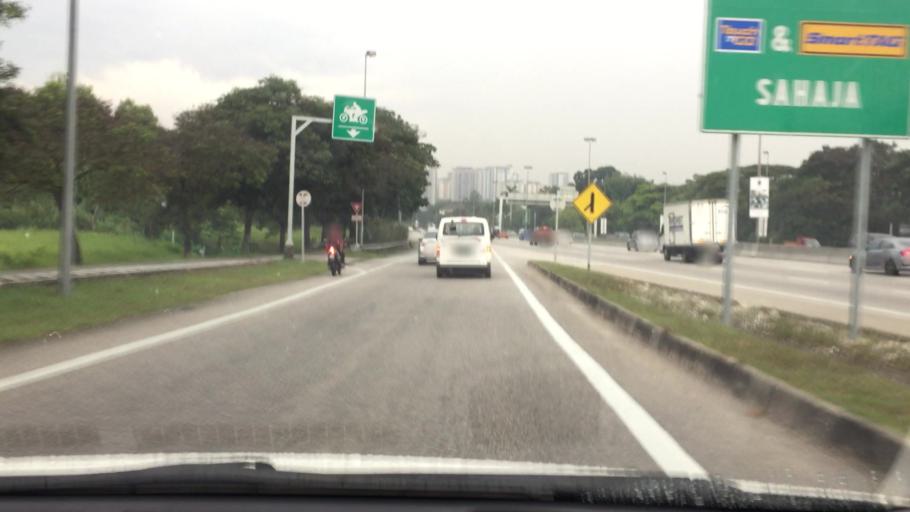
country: MY
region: Selangor
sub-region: Petaling
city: Petaling Jaya
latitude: 3.0689
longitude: 101.6396
